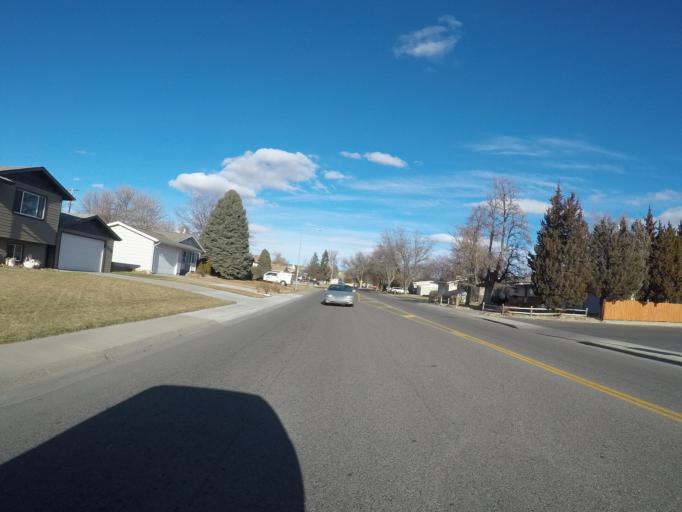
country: US
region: Montana
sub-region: Yellowstone County
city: Billings
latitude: 45.7704
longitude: -108.5648
